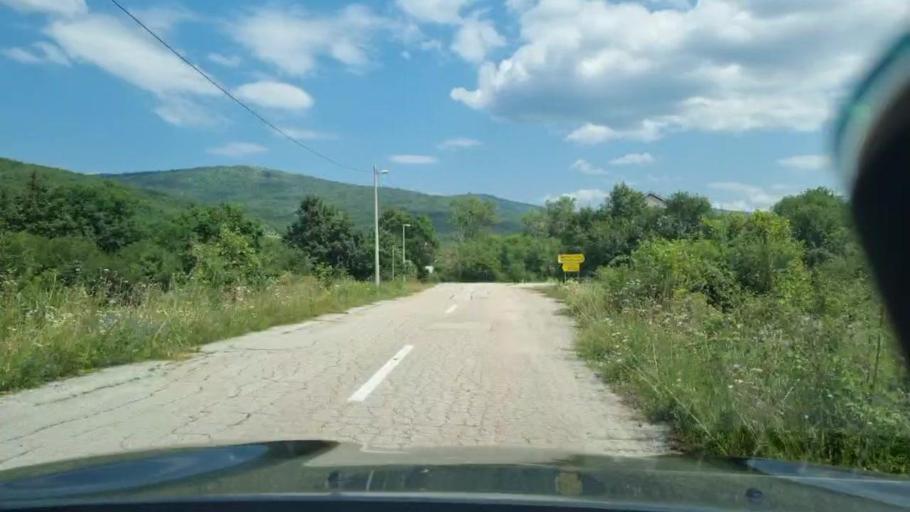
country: BA
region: Federation of Bosnia and Herzegovina
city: Bosansko Grahovo
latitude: 44.2955
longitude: 16.3015
